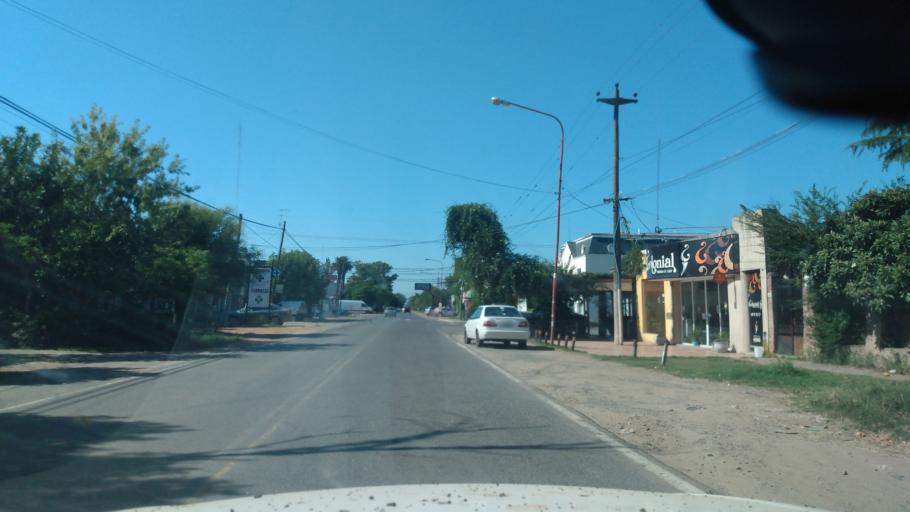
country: AR
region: Buenos Aires
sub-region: Partido de Lujan
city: Lujan
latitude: -34.4900
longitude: -59.0785
